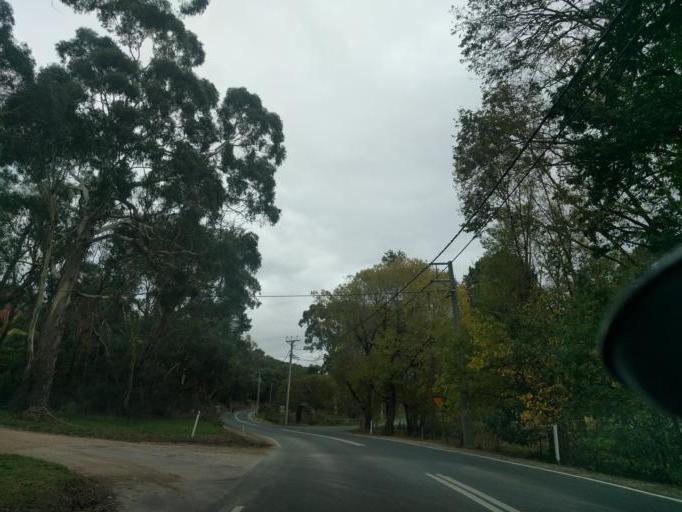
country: AU
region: South Australia
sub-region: Adelaide Hills
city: Stirling
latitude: -35.0394
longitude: 138.7617
